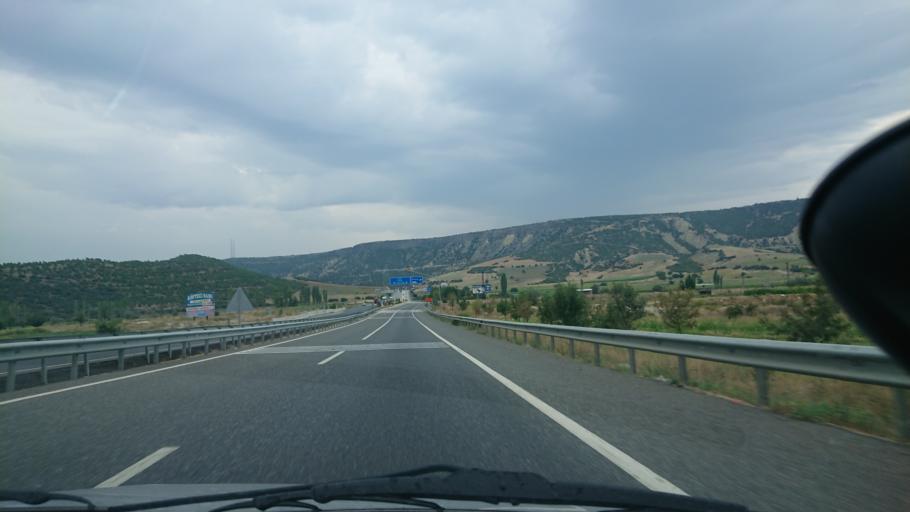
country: TR
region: Manisa
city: Selendi
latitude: 38.6216
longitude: 28.8446
